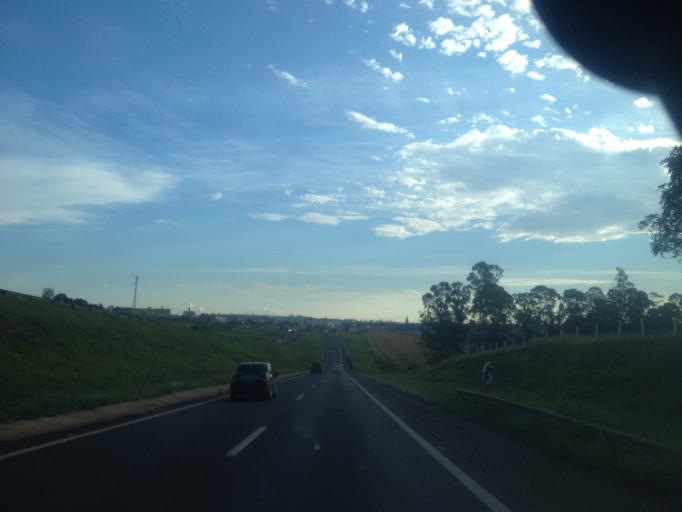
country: BR
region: Sao Paulo
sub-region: Araras
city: Araras
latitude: -22.3388
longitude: -47.3913
